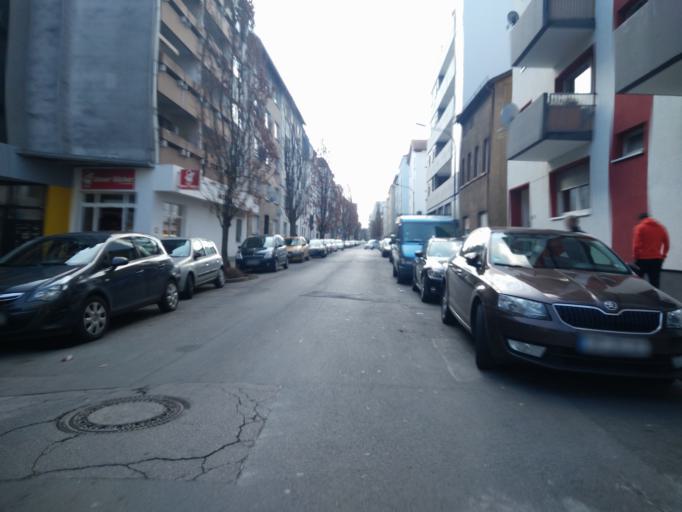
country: DE
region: Hesse
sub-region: Regierungsbezirk Darmstadt
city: Offenbach
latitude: 50.1109
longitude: 8.7530
